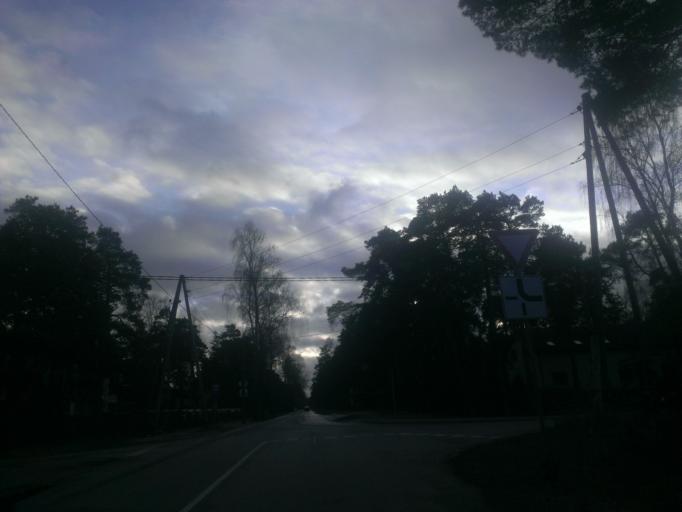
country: LV
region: Riga
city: Bolderaja
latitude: 57.0711
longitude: 24.1049
